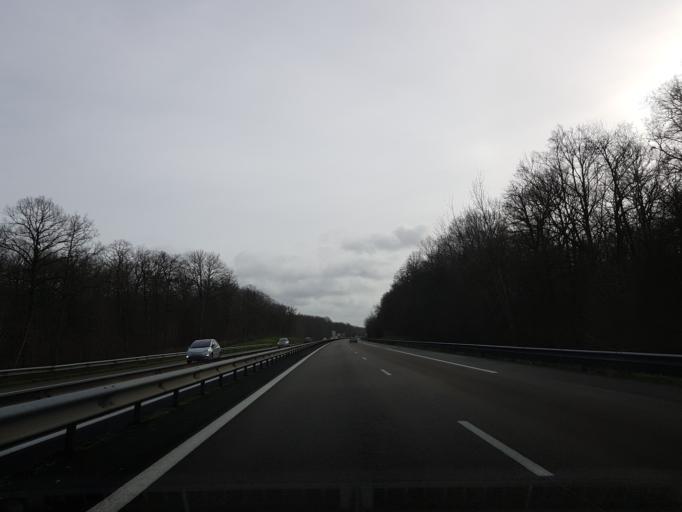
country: FR
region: Champagne-Ardenne
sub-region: Departement de l'Aube
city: Lusigny-sur-Barse
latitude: 48.1949
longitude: 4.2693
